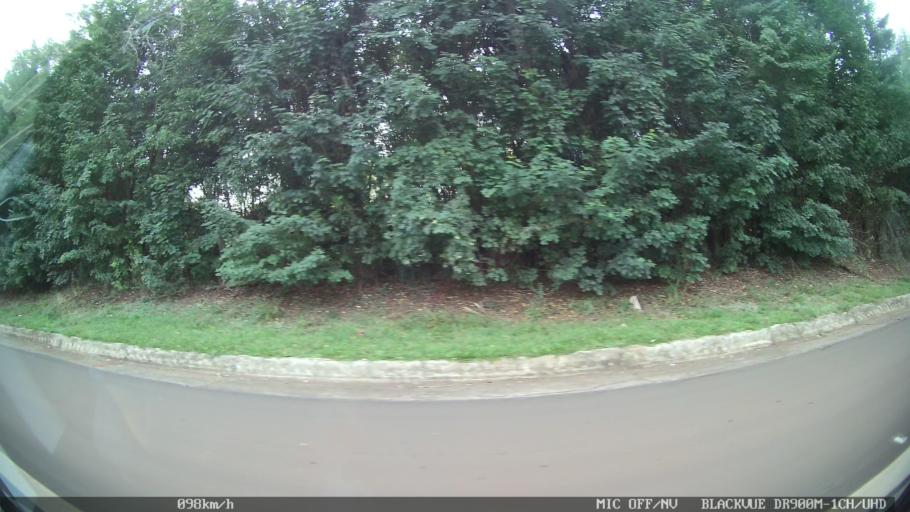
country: BR
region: Sao Paulo
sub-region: Piracicaba
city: Piracicaba
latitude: -22.6990
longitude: -47.5941
